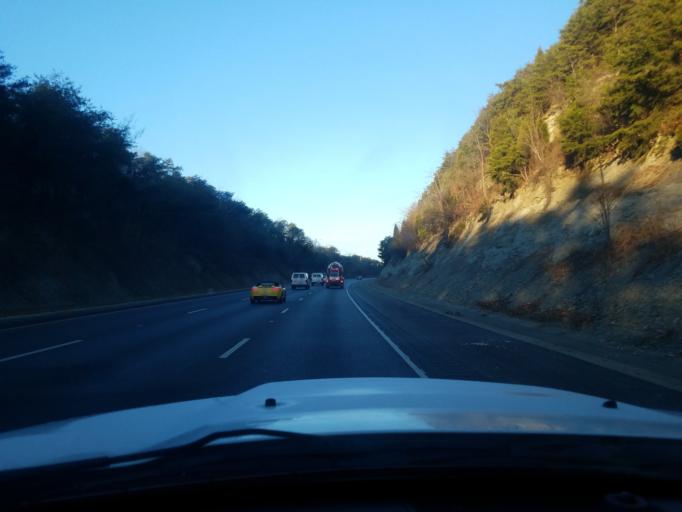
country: US
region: Indiana
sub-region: Floyd County
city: New Albany
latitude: 38.3016
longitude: -85.8684
